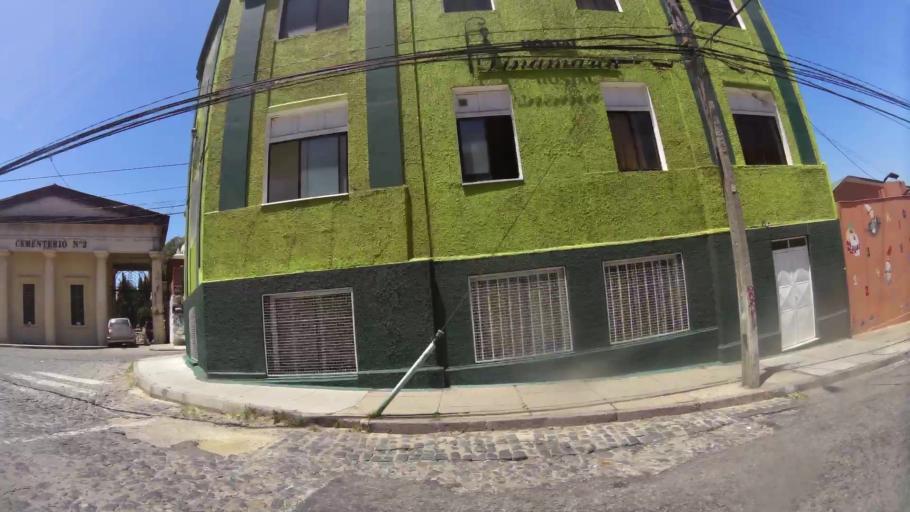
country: CL
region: Valparaiso
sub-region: Provincia de Valparaiso
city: Valparaiso
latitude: -33.0467
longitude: -71.6269
